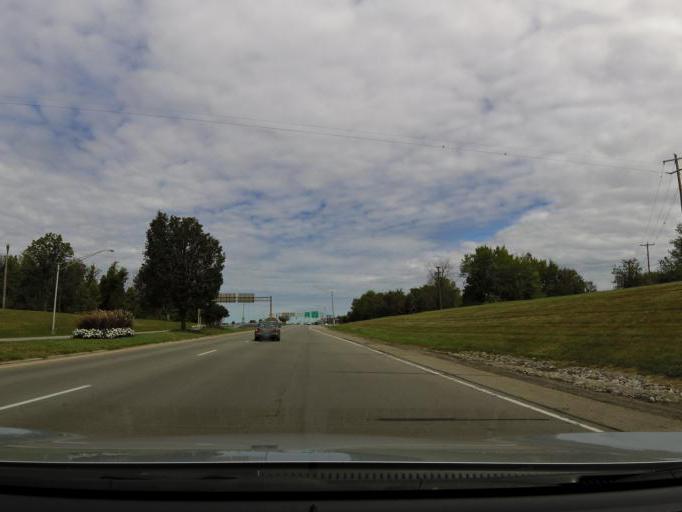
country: US
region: Kentucky
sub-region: Boone County
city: Hebron
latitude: 39.0657
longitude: -84.6562
